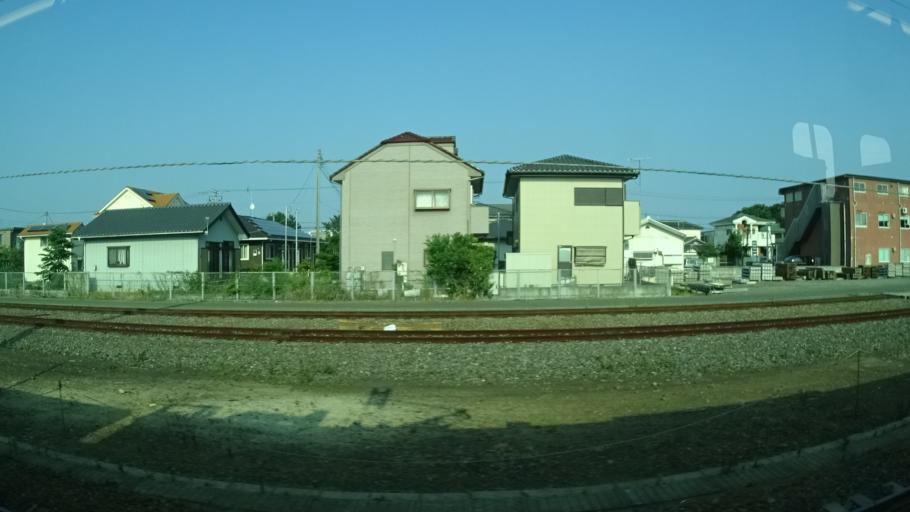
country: JP
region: Ibaraki
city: Takahagi
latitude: 36.7098
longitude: 140.7167
